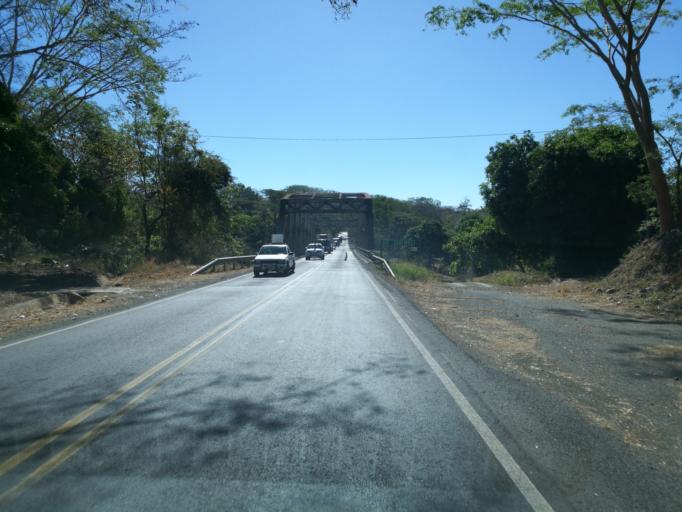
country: CR
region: Puntarenas
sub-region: Canton Central de Puntarenas
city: Puntarenas
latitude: 10.1033
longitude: -84.8751
